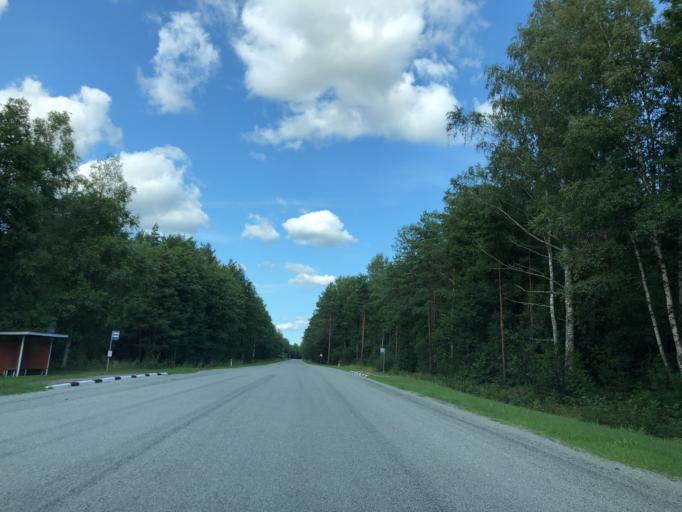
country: EE
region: Hiiumaa
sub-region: Kaerdla linn
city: Kardla
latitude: 58.8137
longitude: 22.7346
